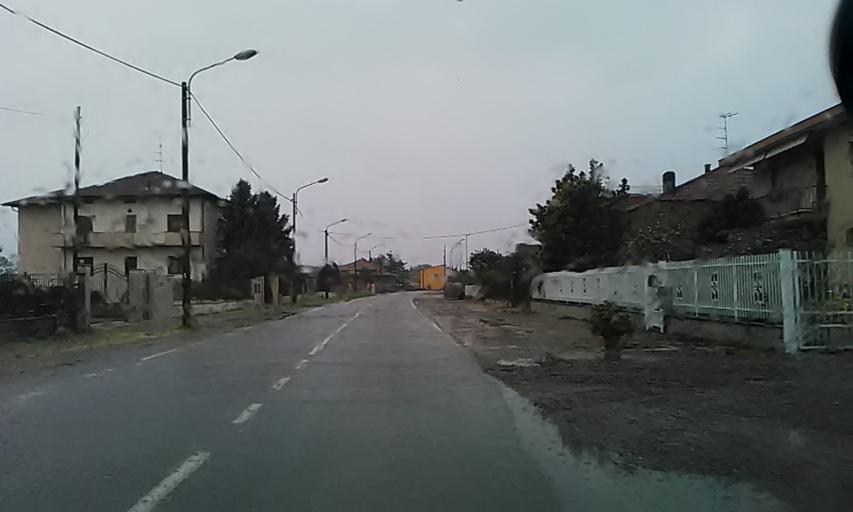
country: IT
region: Piedmont
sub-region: Provincia di Vercelli
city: Arborio
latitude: 45.4950
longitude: 8.3851
